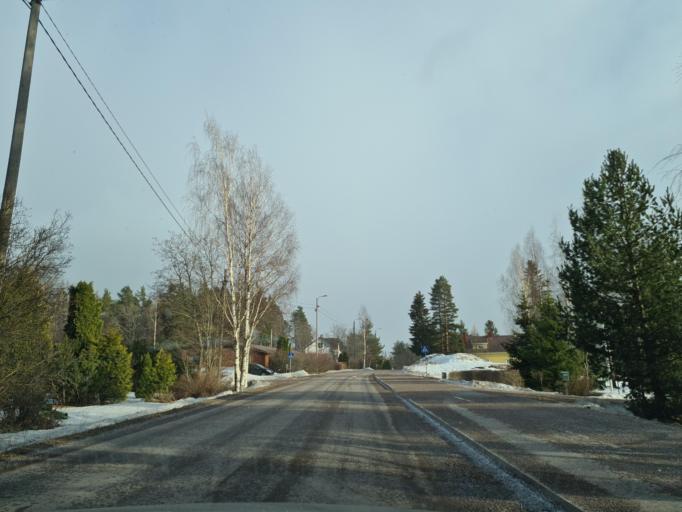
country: FI
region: Uusimaa
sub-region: Helsinki
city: Maentsaelae
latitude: 60.6410
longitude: 25.3093
